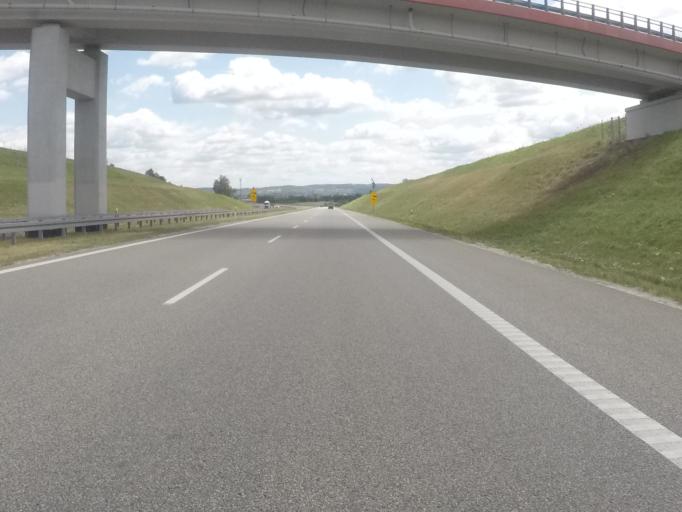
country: PL
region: Subcarpathian Voivodeship
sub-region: Powiat debicki
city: Zyrakow
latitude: 50.0823
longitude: 21.3600
